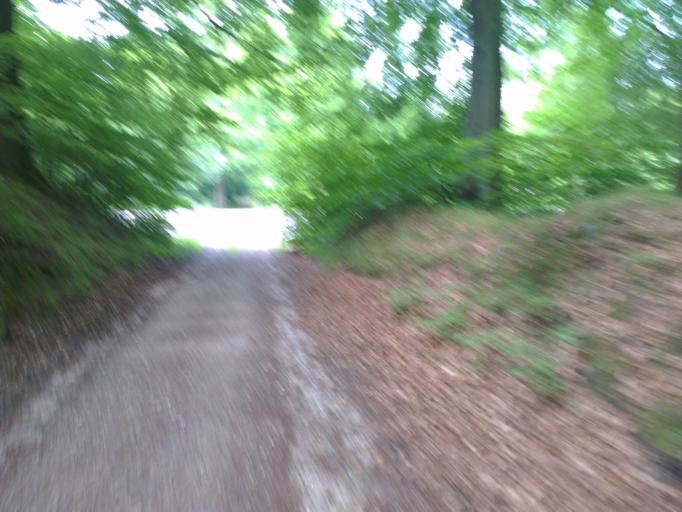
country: DK
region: Capital Region
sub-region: Allerod Kommune
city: Lillerod
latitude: 55.9084
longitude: 12.3475
